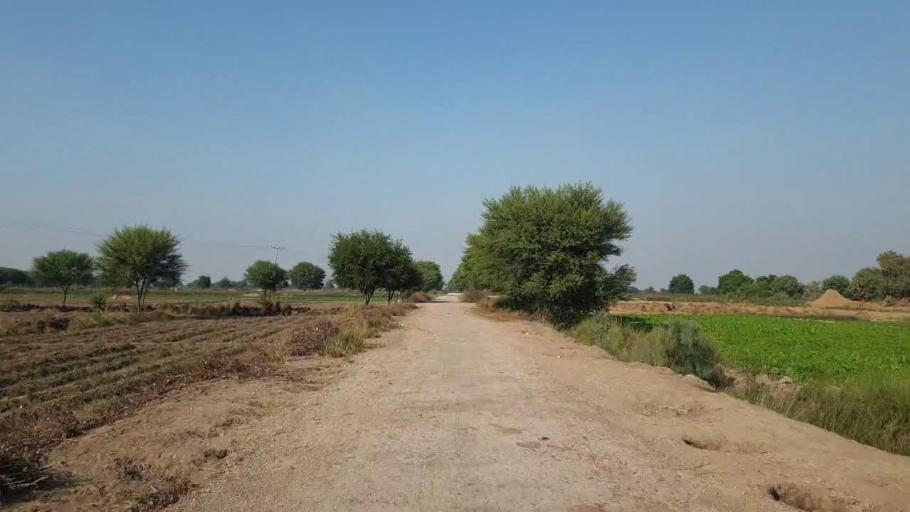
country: PK
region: Sindh
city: Sehwan
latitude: 26.4553
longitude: 67.8158
